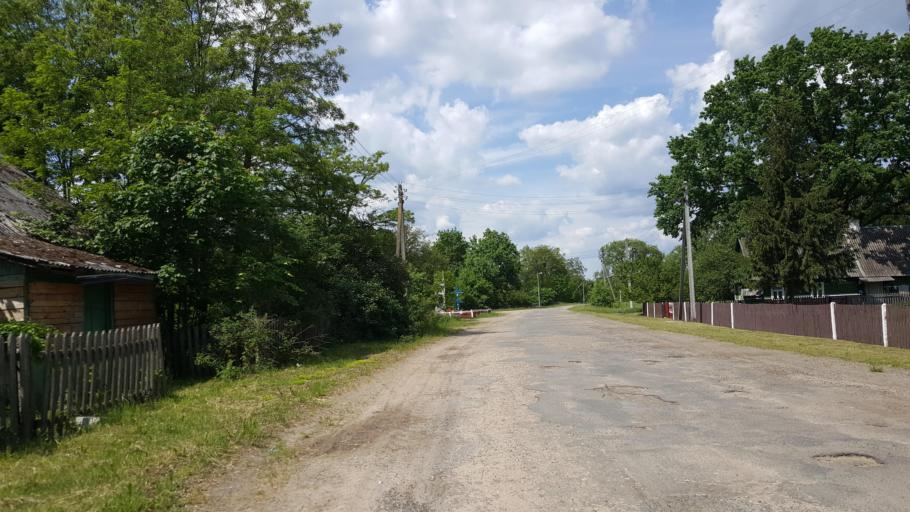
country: BY
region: Brest
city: Zhabinka
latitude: 52.4773
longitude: 24.1410
